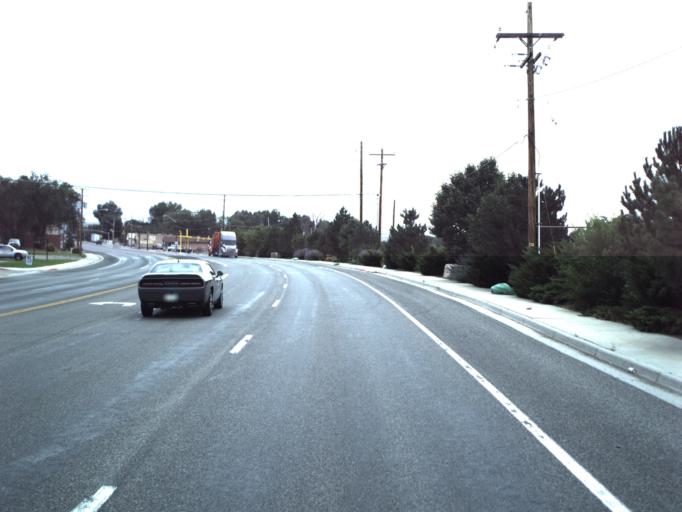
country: US
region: Utah
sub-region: Carbon County
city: Wellington
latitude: 39.5426
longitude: -110.7394
